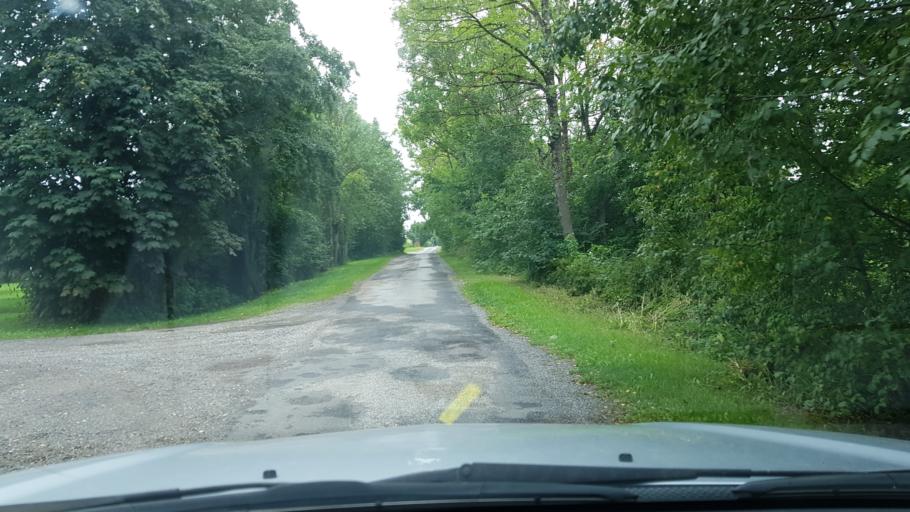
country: EE
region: Harju
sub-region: Joelaehtme vald
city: Loo
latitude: 59.4096
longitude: 24.9440
